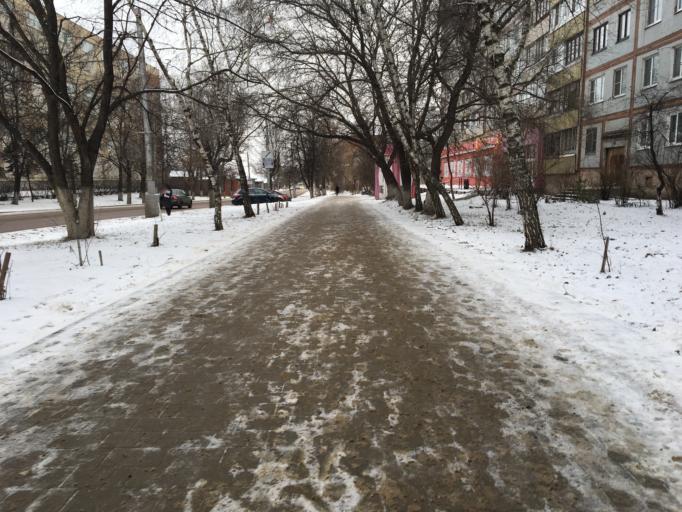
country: RU
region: Tula
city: Tula
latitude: 54.2079
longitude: 37.6078
